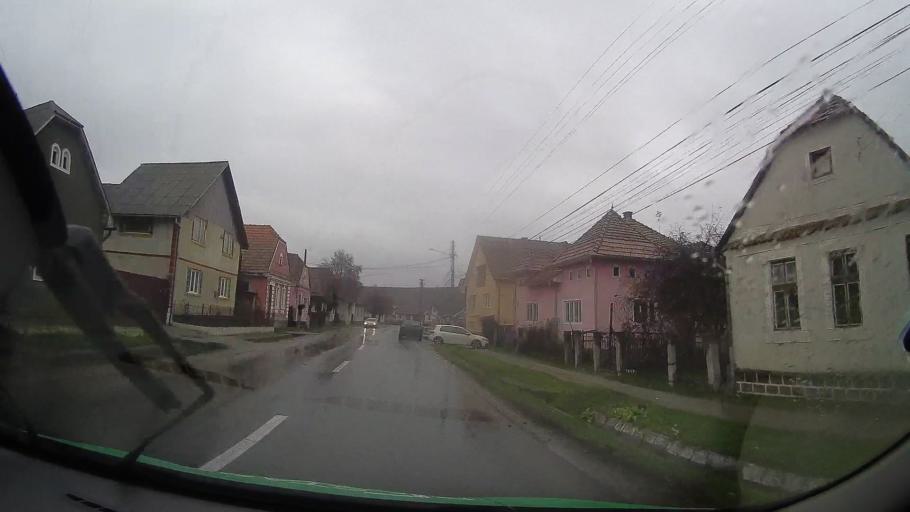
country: RO
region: Bistrita-Nasaud
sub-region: Comuna Mariselu
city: Mariselu
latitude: 47.0381
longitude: 24.4746
